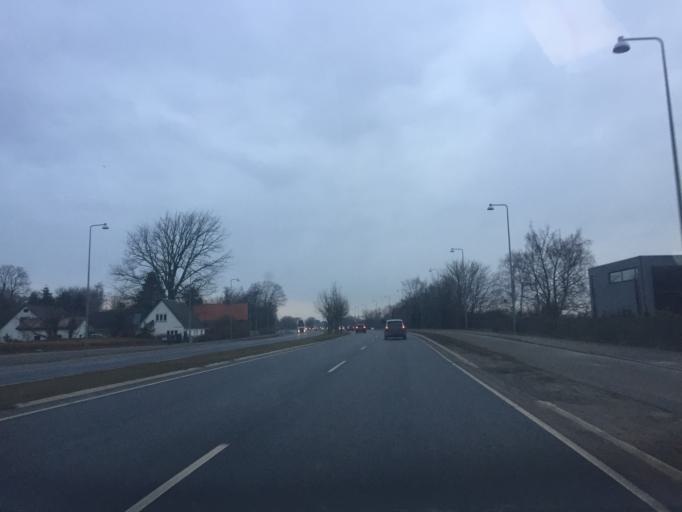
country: DK
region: Zealand
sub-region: Solrod Kommune
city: Solrod Strand
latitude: 55.5069
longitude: 12.2015
